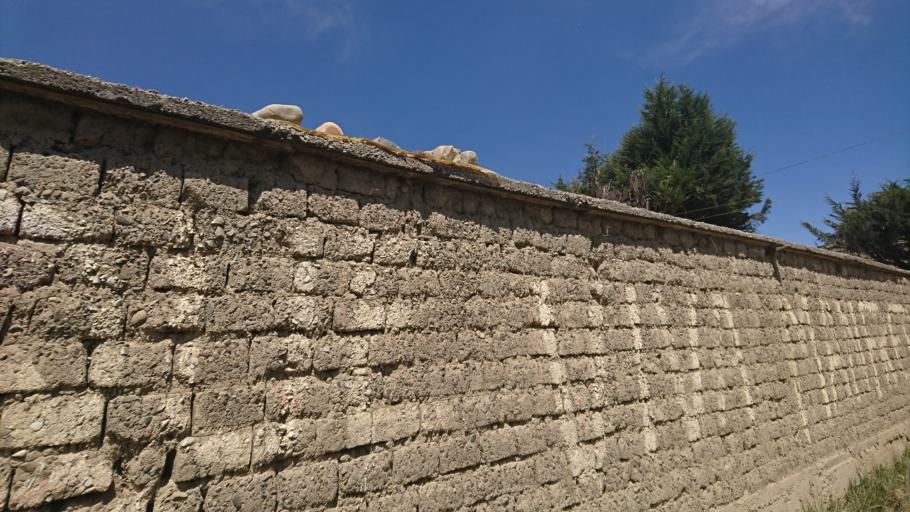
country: BO
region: La Paz
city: La Paz
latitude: -16.4900
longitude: -68.0803
